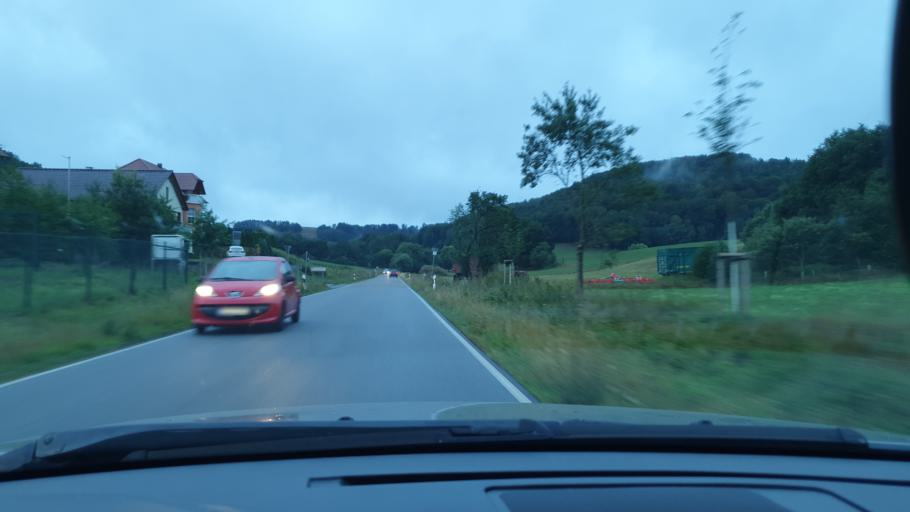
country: DE
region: Rheinland-Pfalz
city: Oberarnbach
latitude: 49.3828
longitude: 7.5847
